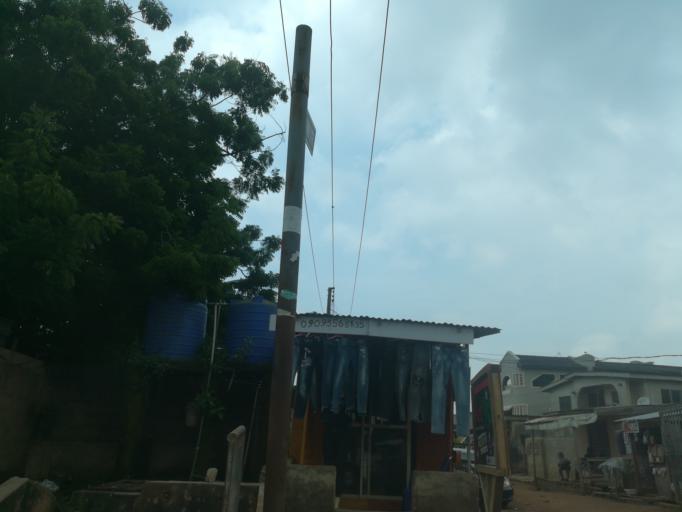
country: NG
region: Lagos
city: Ikorodu
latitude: 6.6169
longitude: 3.5212
